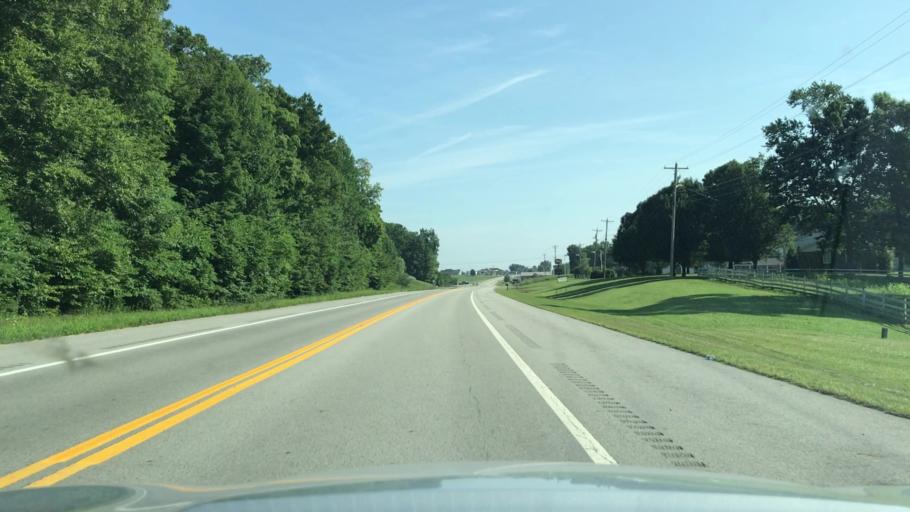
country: US
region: Tennessee
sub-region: Pickett County
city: Byrdstown
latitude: 36.5583
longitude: -85.1676
